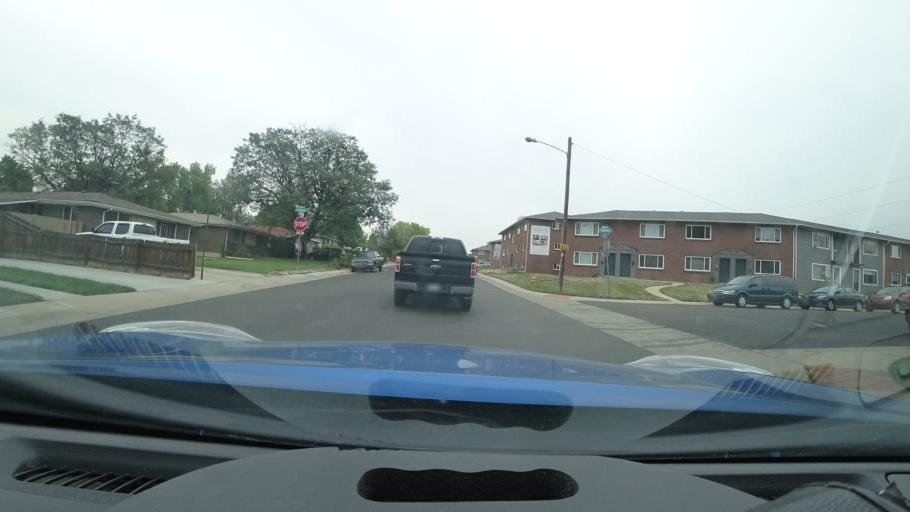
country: US
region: Colorado
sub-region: Arapahoe County
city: Glendale
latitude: 39.6804
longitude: -104.9264
